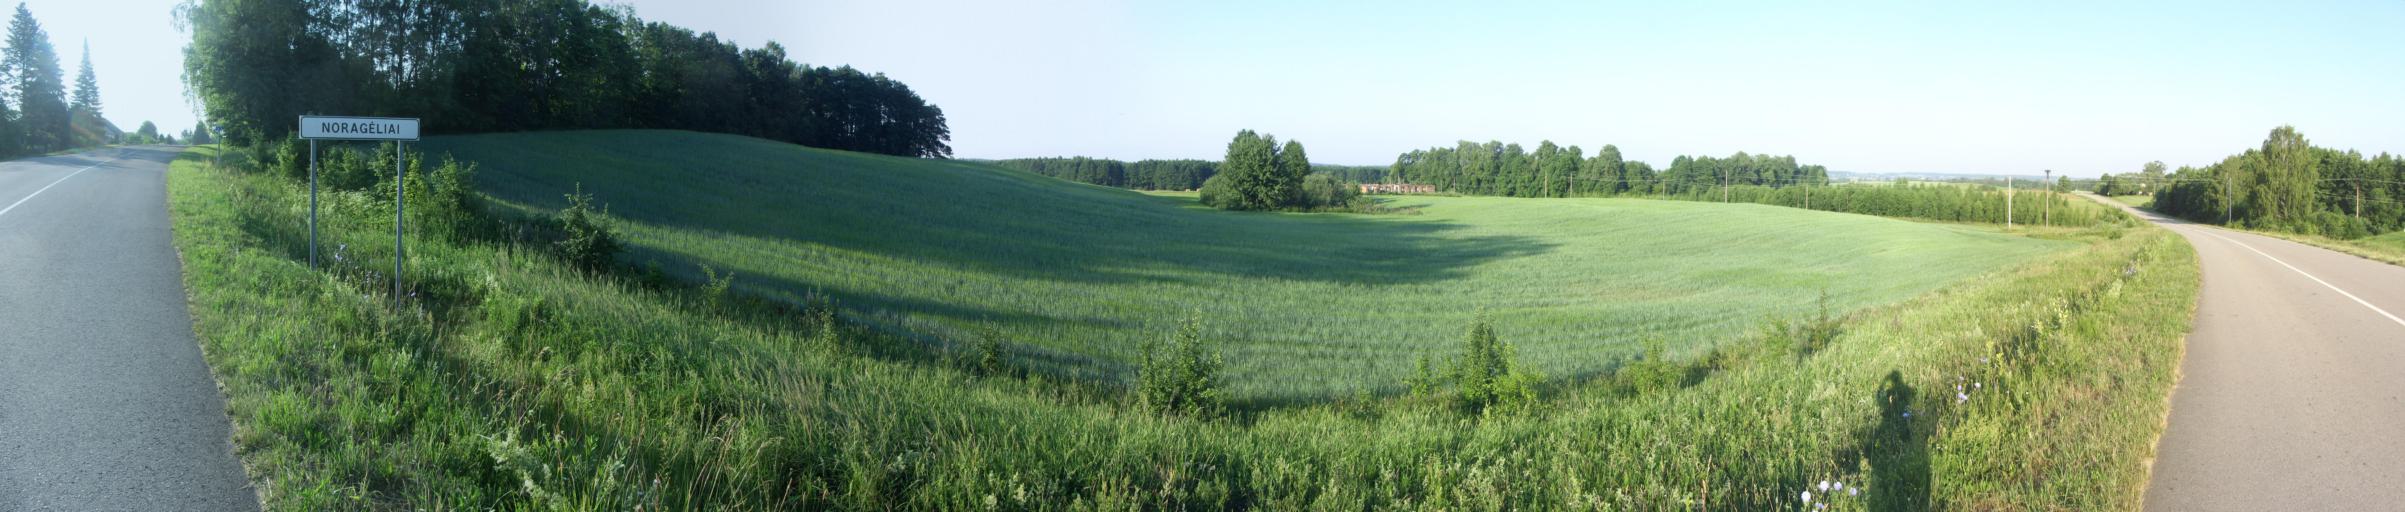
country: LT
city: Veisiejai
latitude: 54.2452
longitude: 23.8790
